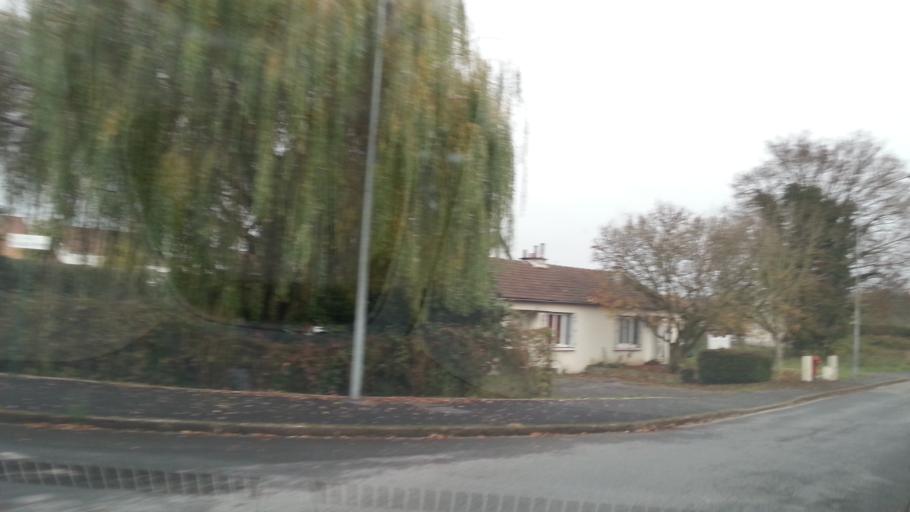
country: FR
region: Picardie
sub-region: Departement de l'Oise
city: Villers-sous-Saint-Leu
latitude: 49.2147
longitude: 2.4130
